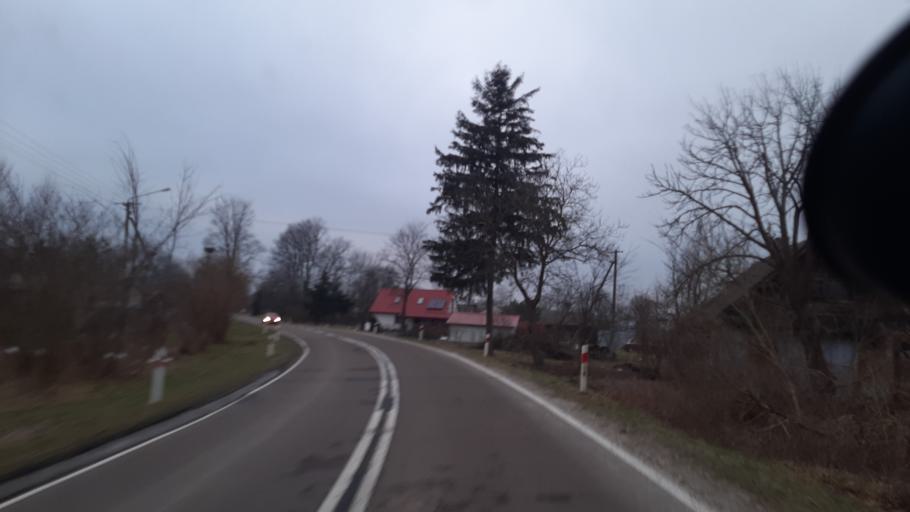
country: PL
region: Lublin Voivodeship
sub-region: Powiat parczewski
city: Podedworze
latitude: 51.5915
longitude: 23.1970
